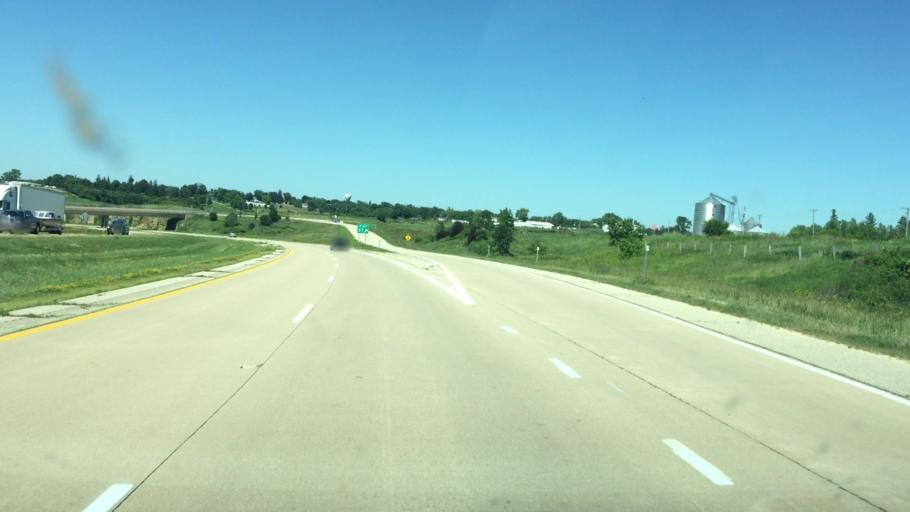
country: US
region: Wisconsin
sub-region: Iowa County
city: Mineral Point
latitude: 42.8446
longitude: -90.1998
